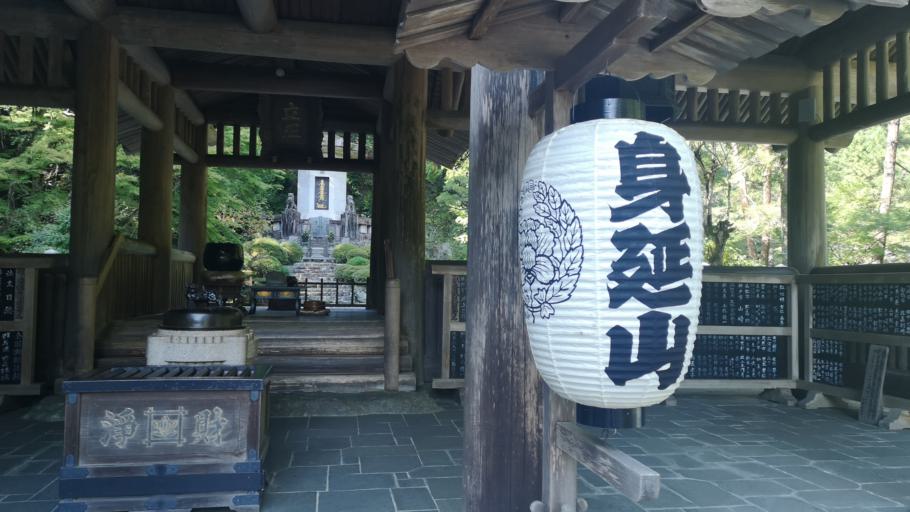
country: JP
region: Shizuoka
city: Fujinomiya
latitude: 35.3818
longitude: 138.4191
